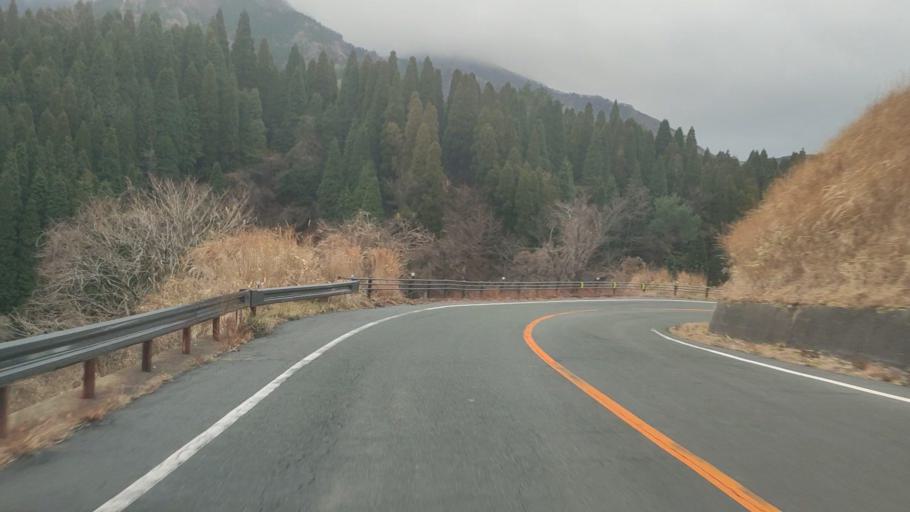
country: JP
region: Kumamoto
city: Aso
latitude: 32.9045
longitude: 131.1454
